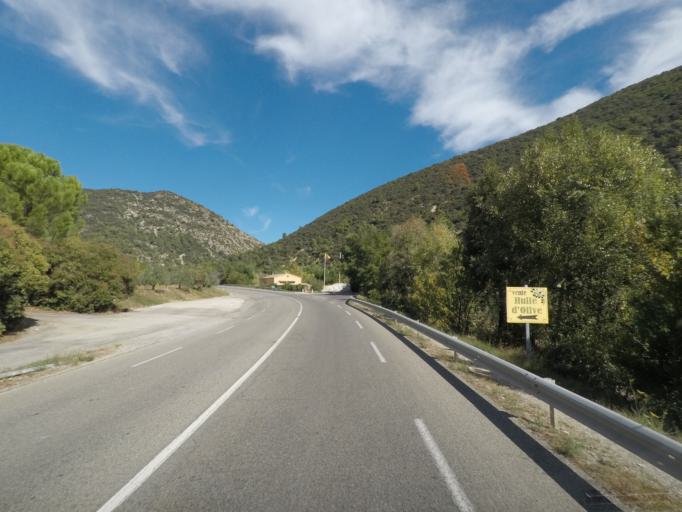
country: FR
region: Rhone-Alpes
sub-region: Departement de la Drome
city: Nyons
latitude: 44.3644
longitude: 5.1531
